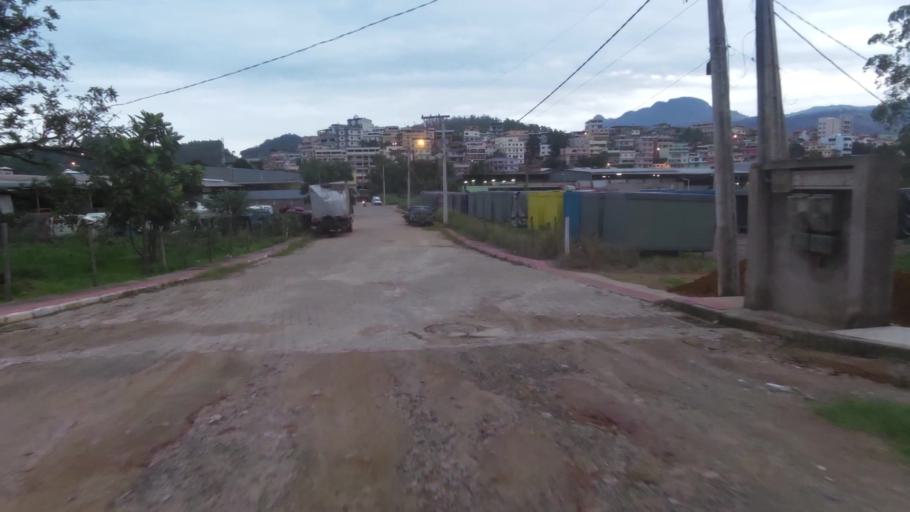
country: BR
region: Espirito Santo
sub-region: Iconha
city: Iconha
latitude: -20.7913
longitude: -40.8075
